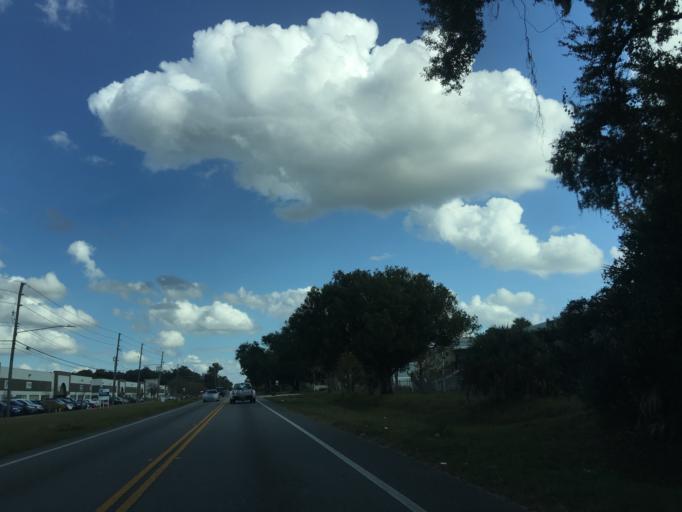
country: US
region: Florida
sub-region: Orange County
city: Eatonville
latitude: 28.6185
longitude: -81.4062
